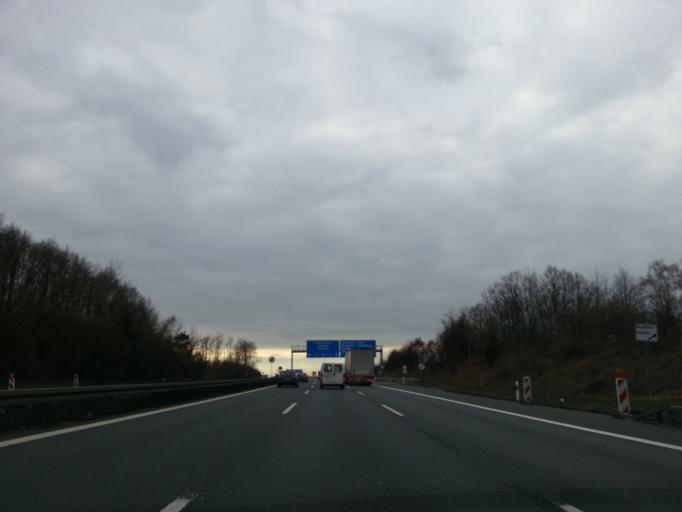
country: DE
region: Bavaria
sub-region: Regierungsbezirk Unterfranken
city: Mainstockheim
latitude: 49.7850
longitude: 10.1209
